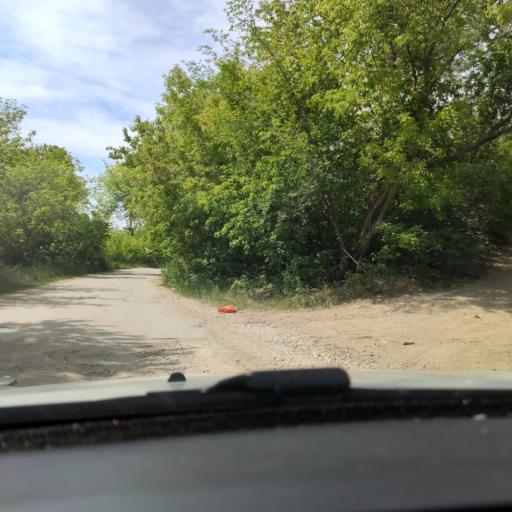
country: RU
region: Samara
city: Volzhskiy
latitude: 53.3441
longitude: 50.2021
